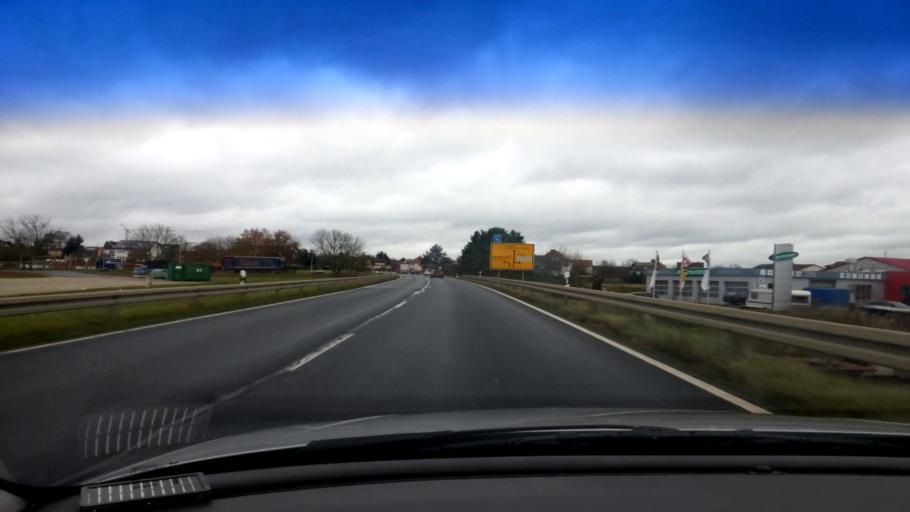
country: DE
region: Bavaria
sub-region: Upper Franconia
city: Rattelsdorf
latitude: 50.0104
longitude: 10.8909
